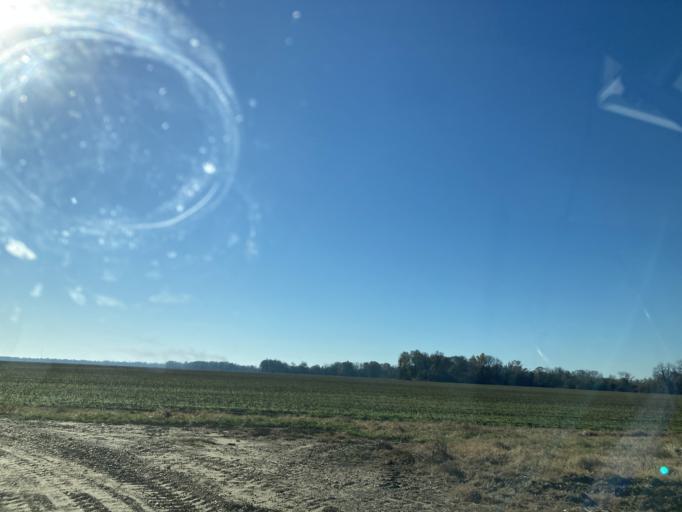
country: US
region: Mississippi
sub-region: Sharkey County
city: Rolling Fork
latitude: 32.8576
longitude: -90.6941
